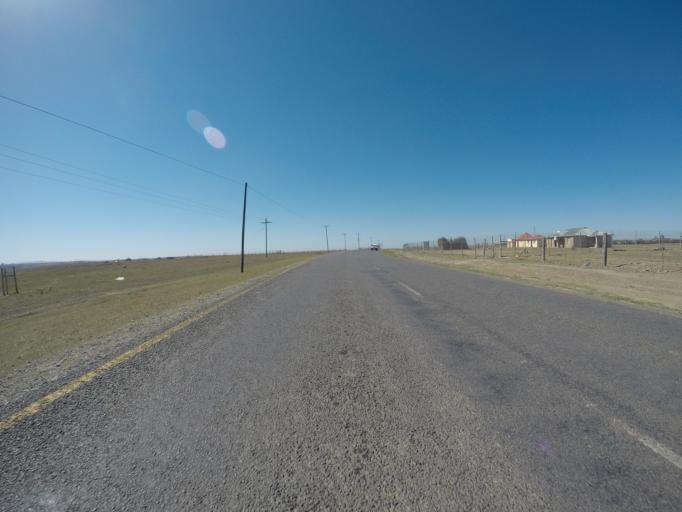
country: ZA
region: Eastern Cape
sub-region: OR Tambo District Municipality
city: Mthatha
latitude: -31.8870
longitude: 28.7617
